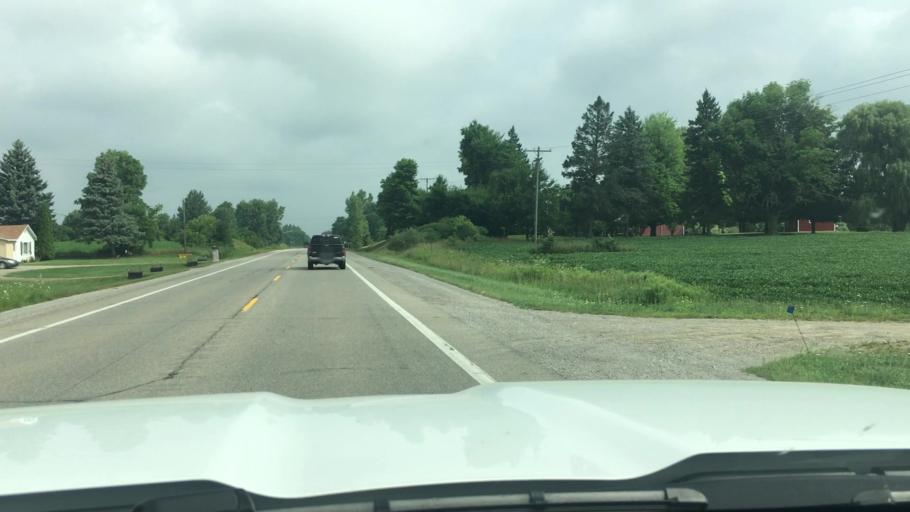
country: US
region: Michigan
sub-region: Lapeer County
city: Imlay City
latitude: 43.1192
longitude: -83.0729
